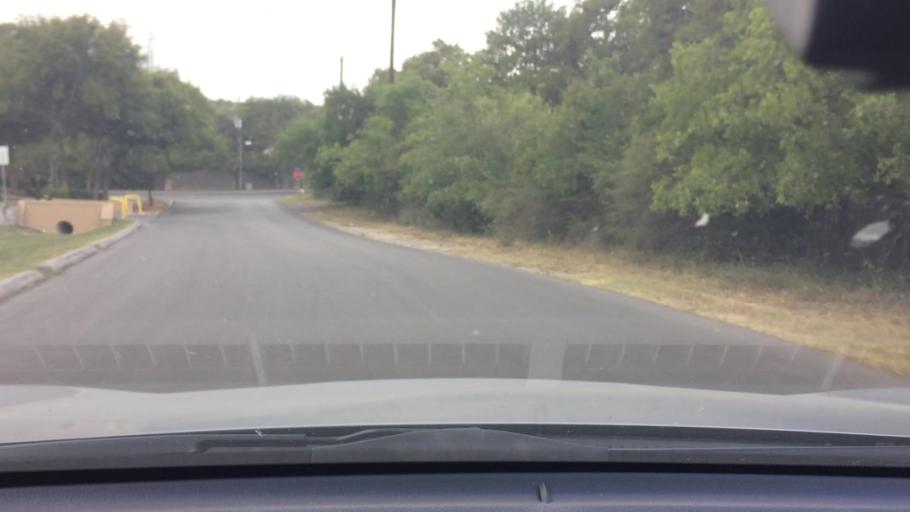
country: US
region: Texas
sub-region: Bexar County
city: Hollywood Park
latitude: 29.5588
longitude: -98.4733
